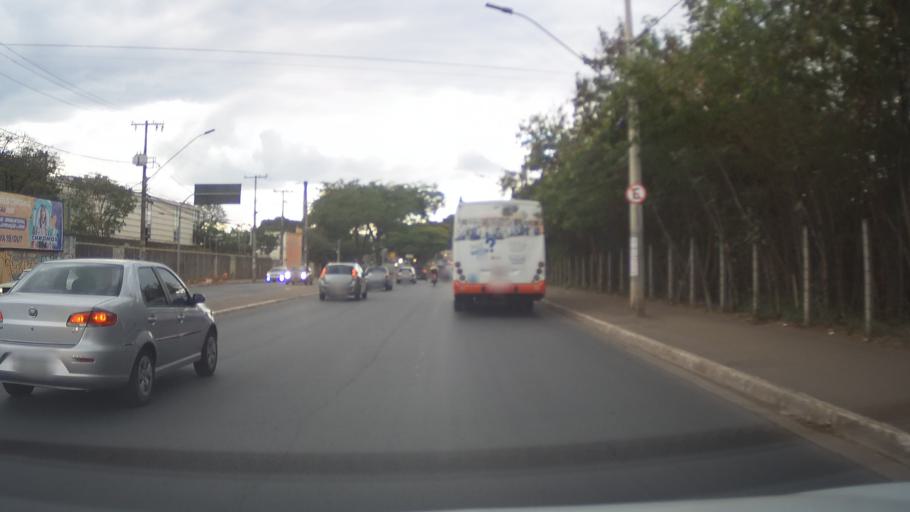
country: BR
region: Minas Gerais
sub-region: Contagem
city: Contagem
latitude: -19.9564
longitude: -44.0166
